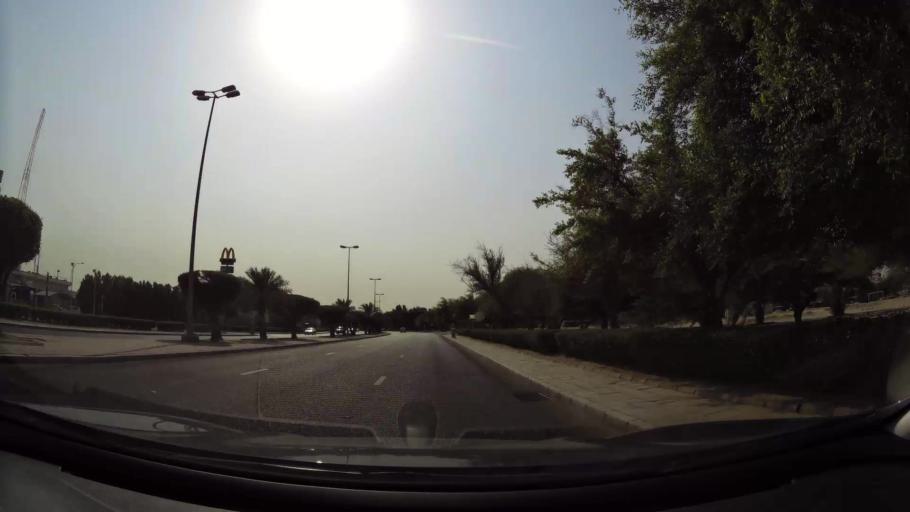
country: KW
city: Bayan
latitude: 29.3001
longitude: 48.0537
